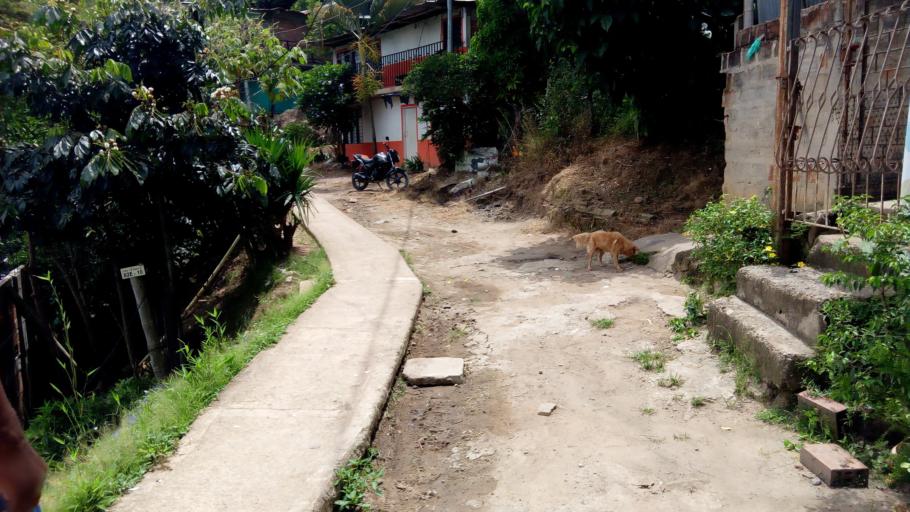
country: CO
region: Valle del Cauca
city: Cali
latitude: 3.3813
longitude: -76.5629
